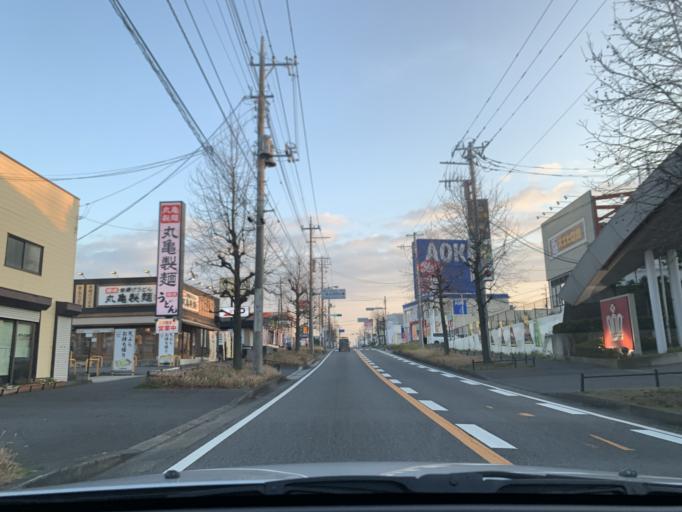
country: JP
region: Chiba
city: Matsudo
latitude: 35.7682
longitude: 139.9106
